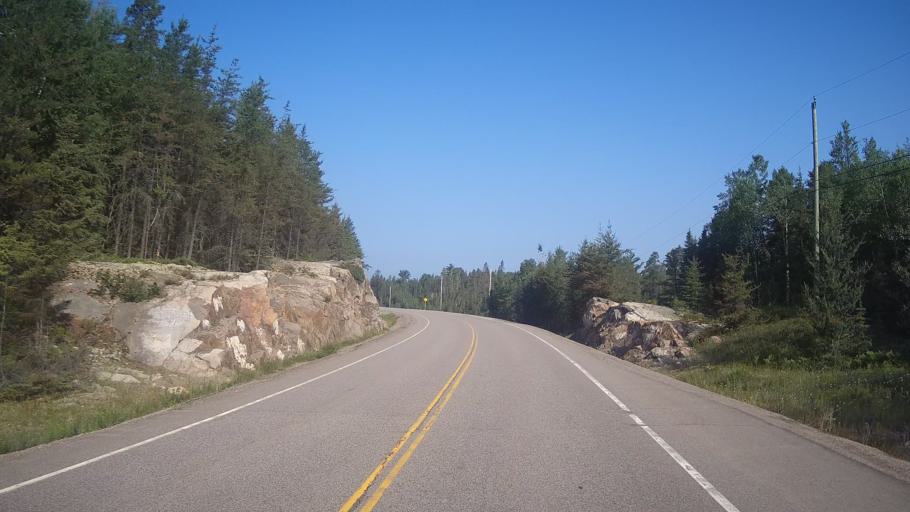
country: CA
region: Ontario
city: Rayside-Balfour
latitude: 46.7299
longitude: -81.5822
